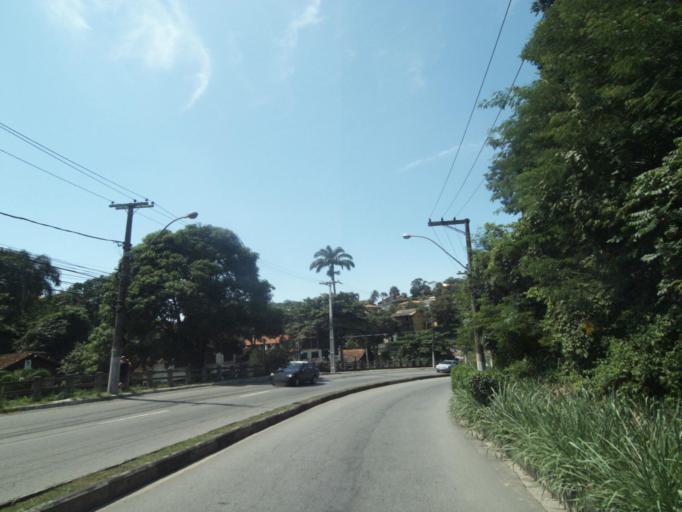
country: BR
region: Rio de Janeiro
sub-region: Niteroi
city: Niteroi
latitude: -22.9034
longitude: -43.0491
